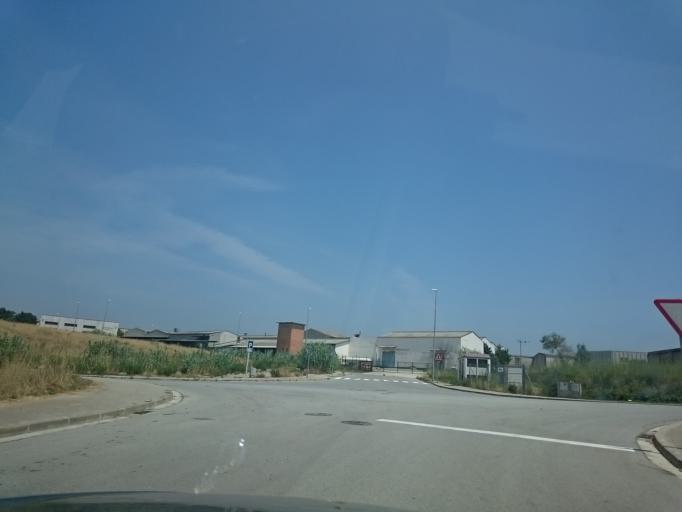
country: ES
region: Catalonia
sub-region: Provincia de Barcelona
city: Avinyonet del Penedes
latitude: 41.3615
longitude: 1.7660
